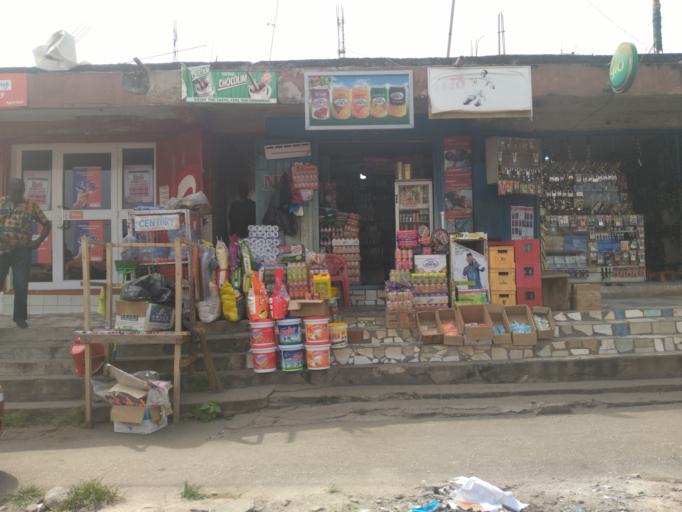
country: GH
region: Ashanti
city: Kumasi
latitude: 6.6847
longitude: -1.6093
